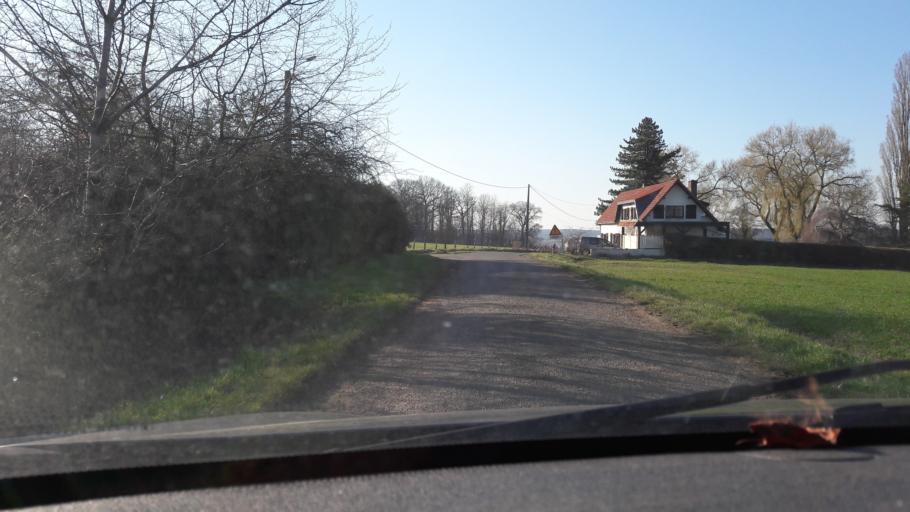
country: BE
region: Wallonia
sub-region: Province du Hainaut
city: Beaumont
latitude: 50.2518
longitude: 4.2071
